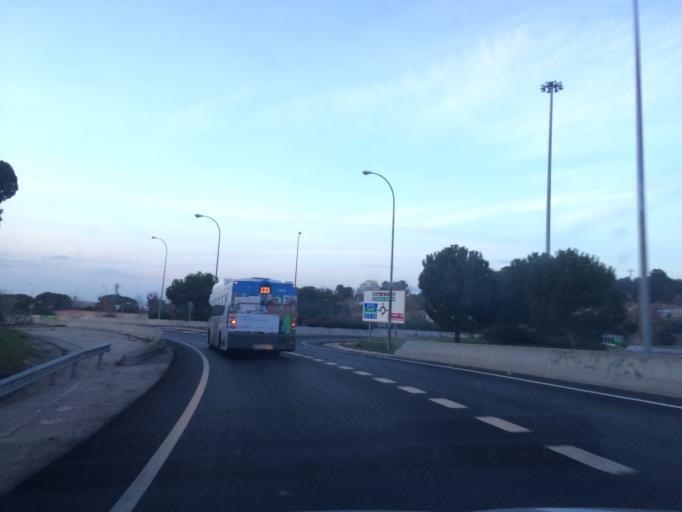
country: ES
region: Madrid
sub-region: Provincia de Madrid
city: Moncloa-Aravaca
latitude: 40.4530
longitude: -3.7399
